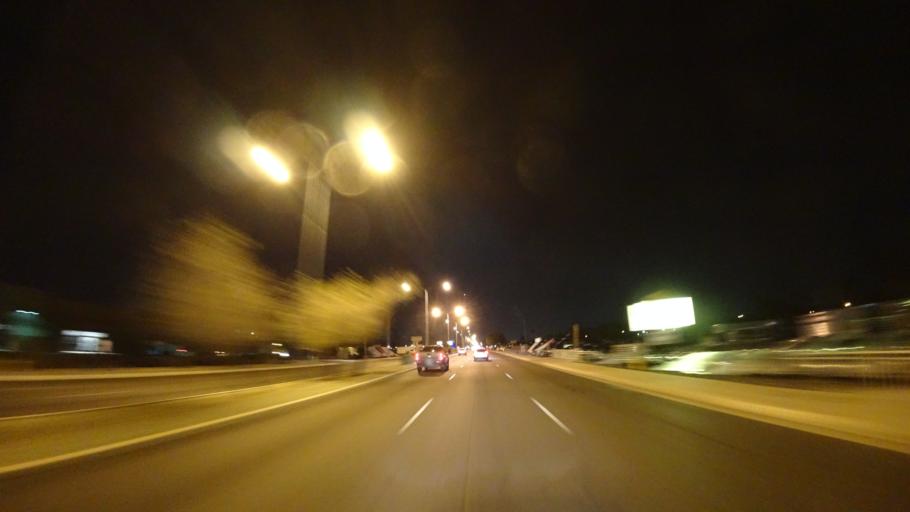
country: US
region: Arizona
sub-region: Maricopa County
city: Mesa
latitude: 33.4156
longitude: -111.7552
